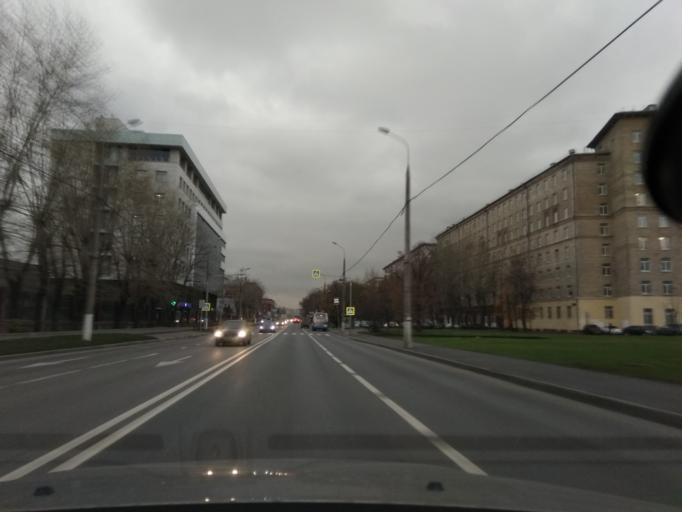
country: RU
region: Moscow
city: Ostankinskiy
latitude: 55.8193
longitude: 37.5936
